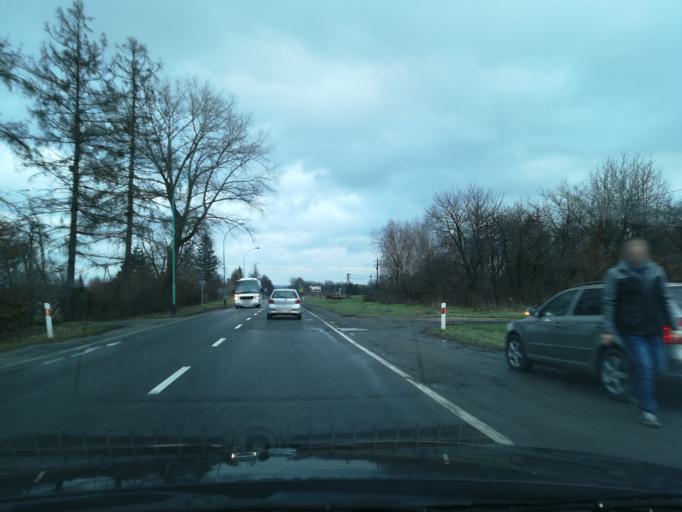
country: PL
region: Subcarpathian Voivodeship
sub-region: Powiat lancucki
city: Gluchow
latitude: 50.0770
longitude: 22.2598
